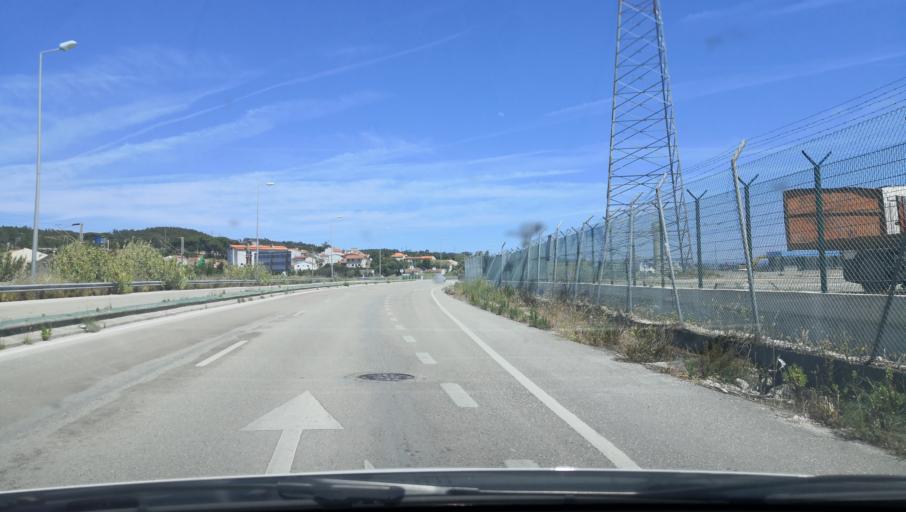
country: PT
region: Coimbra
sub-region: Figueira da Foz
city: Figueira da Foz
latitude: 40.1481
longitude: -8.8405
